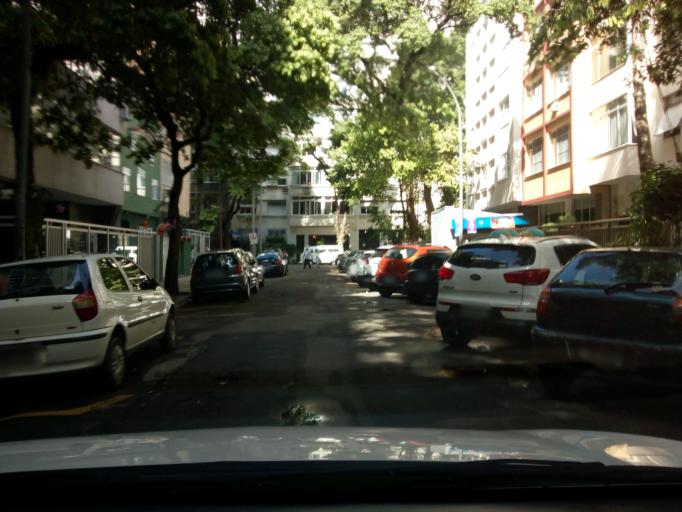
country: BR
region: Rio de Janeiro
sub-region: Rio De Janeiro
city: Rio de Janeiro
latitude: -22.9825
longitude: -43.1938
